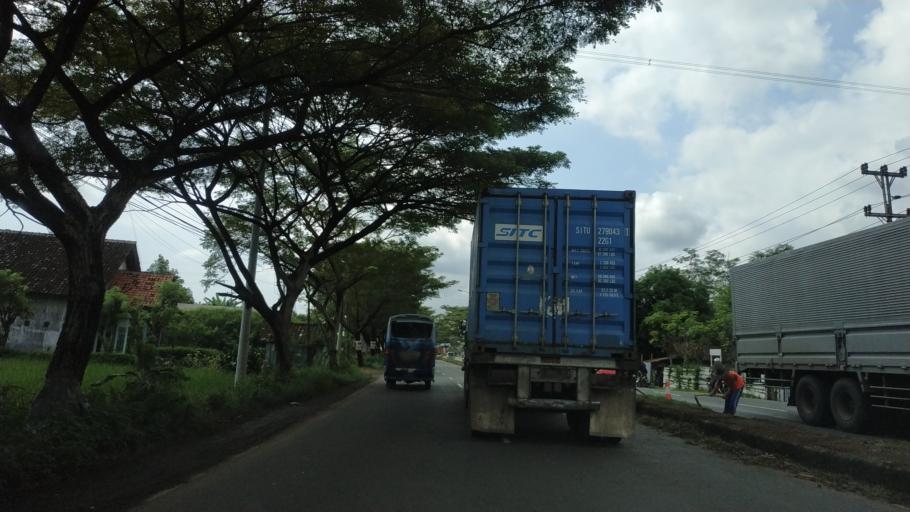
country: ID
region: Central Java
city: Pekalongan
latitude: -6.9506
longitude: 109.7946
